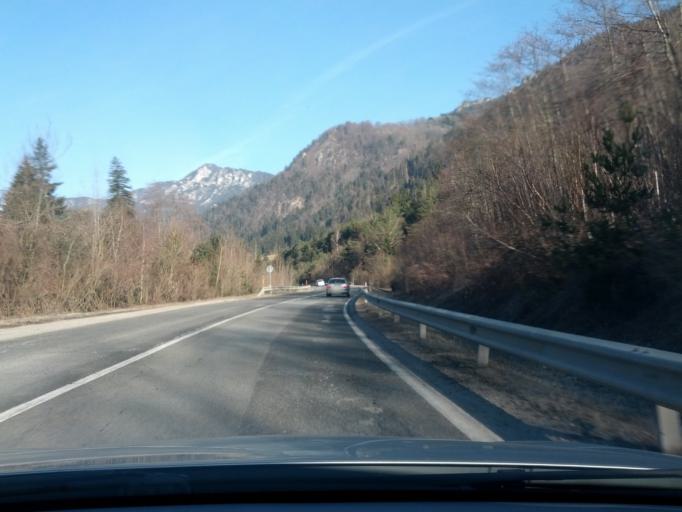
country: SI
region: Jesenice
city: Hrusica
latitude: 46.4519
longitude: 13.9900
